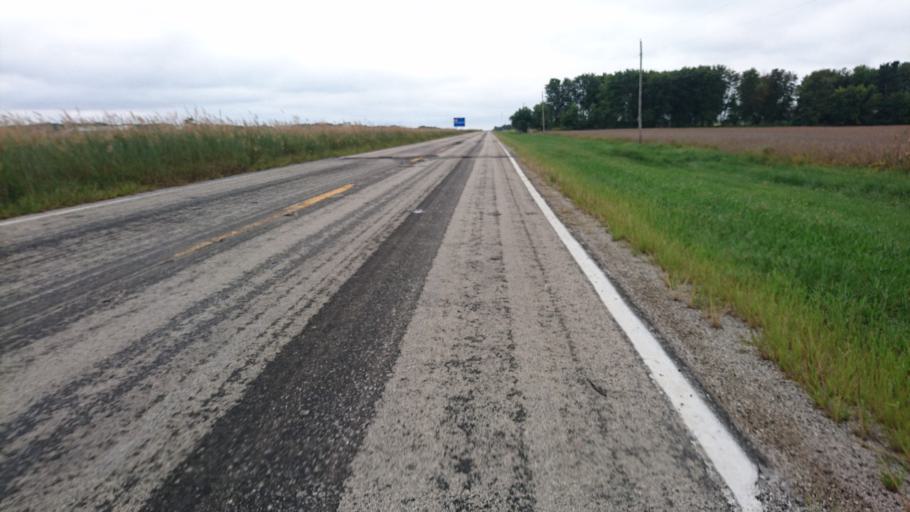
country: US
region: Illinois
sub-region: Montgomery County
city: Raymond
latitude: 39.3061
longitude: -89.6429
